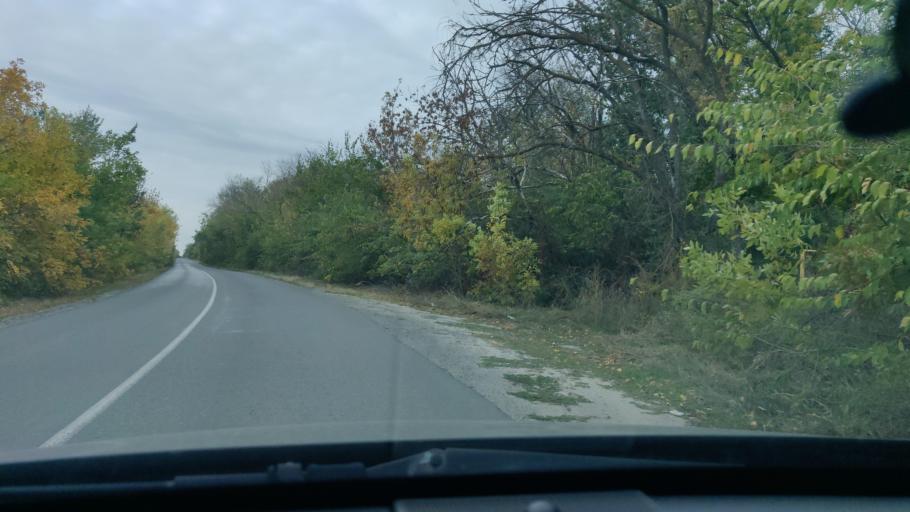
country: RU
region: Rostov
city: Ust'-Donetskiy
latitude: 47.6537
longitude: 40.8938
